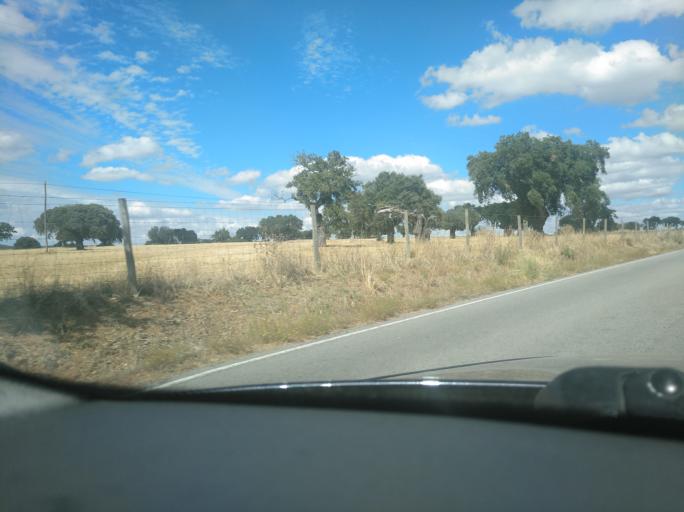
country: PT
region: Portalegre
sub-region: Arronches
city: Arronches
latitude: 39.1419
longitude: -7.2363
